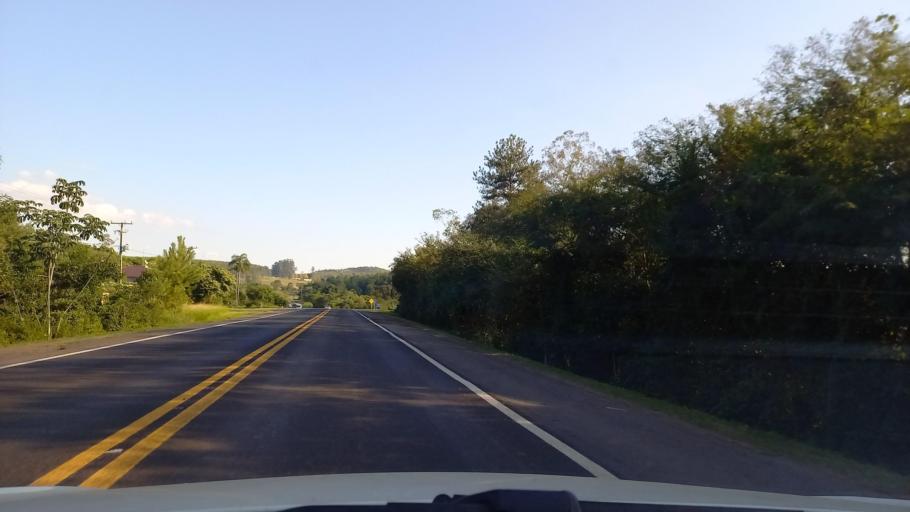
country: BR
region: Rio Grande do Sul
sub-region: Taquari
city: Taquari
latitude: -29.6981
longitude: -51.7503
